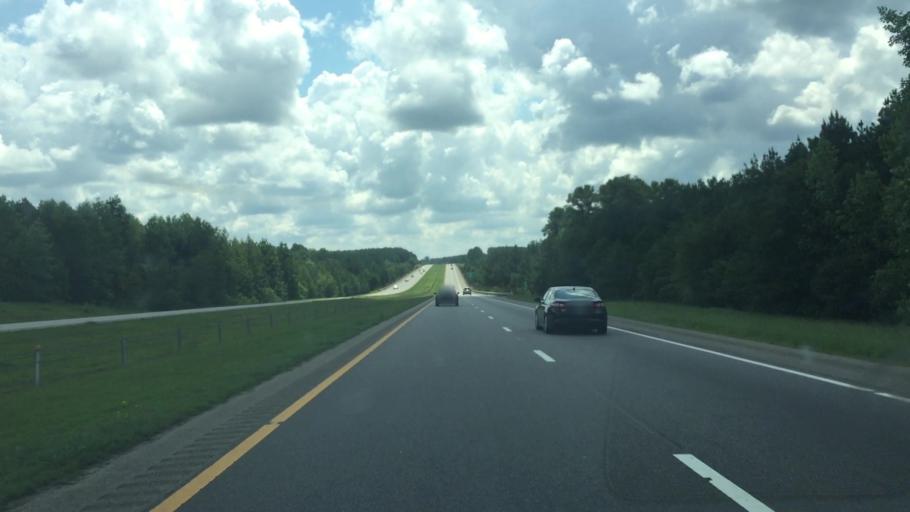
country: US
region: North Carolina
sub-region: Richmond County
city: East Rockingham
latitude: 34.8810
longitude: -79.7798
